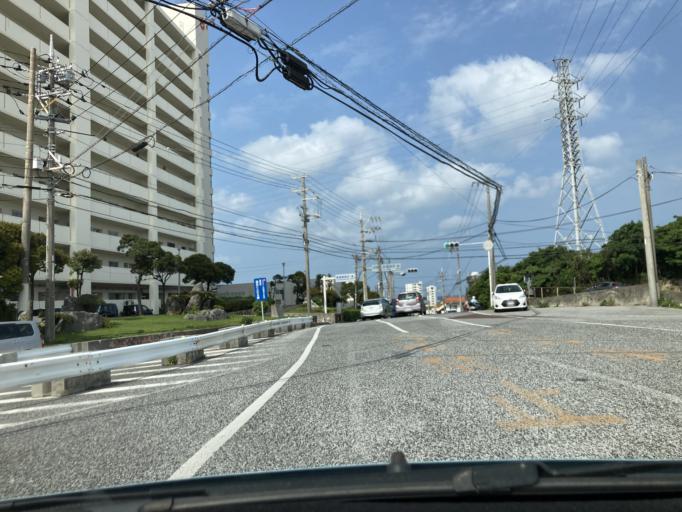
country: JP
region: Okinawa
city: Ginowan
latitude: 26.2686
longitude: 127.7154
